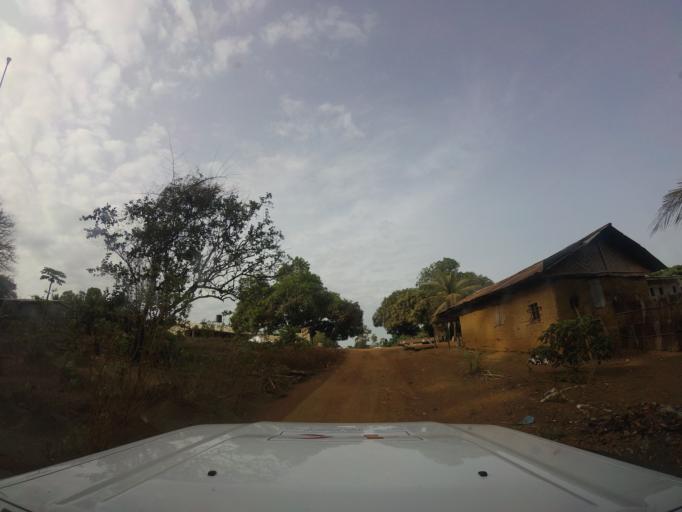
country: LR
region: Grand Cape Mount
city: Robertsport
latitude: 6.9369
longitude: -11.3306
